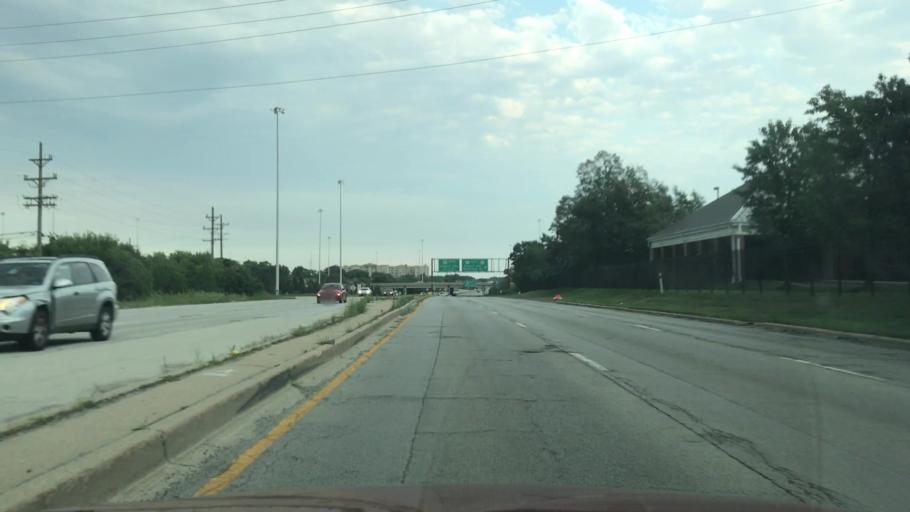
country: US
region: Illinois
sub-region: DuPage County
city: Oakbrook Terrace
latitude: 41.8608
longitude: -87.9640
